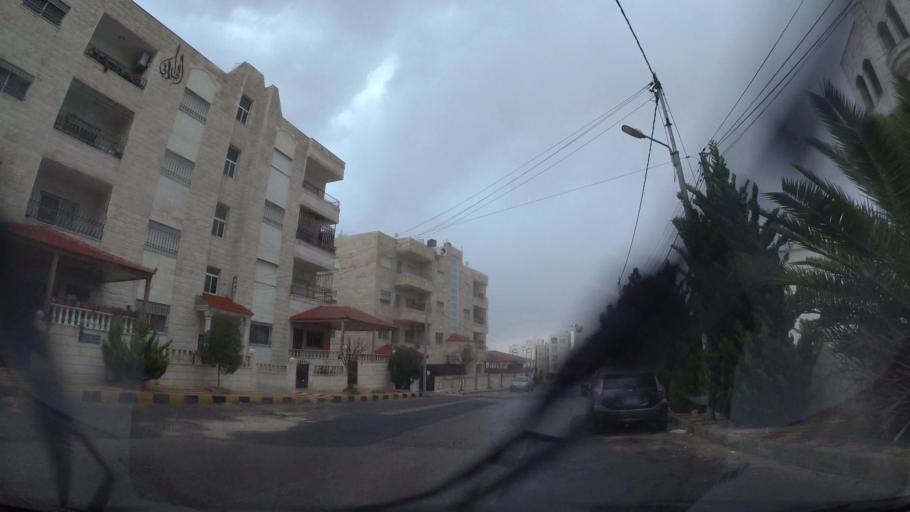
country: JO
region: Amman
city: Amman
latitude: 32.0063
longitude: 35.9569
